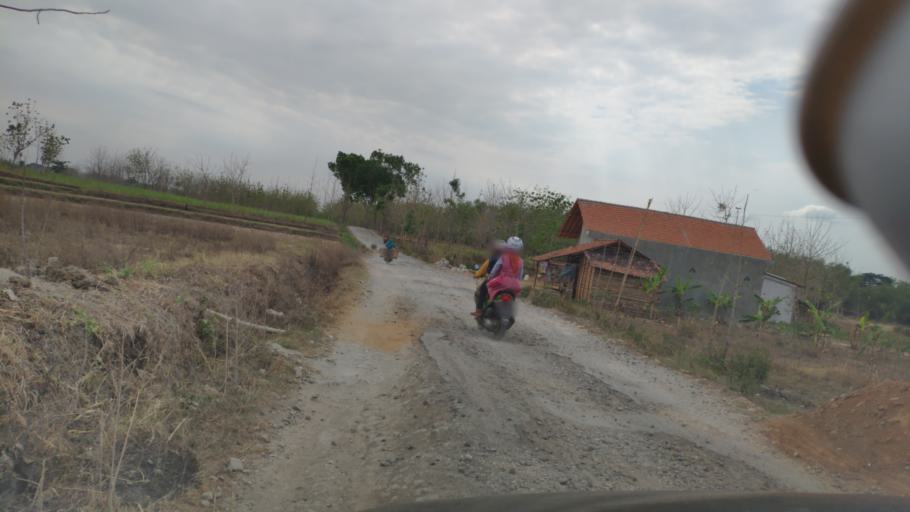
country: ID
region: Central Java
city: Jembangan
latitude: -6.9520
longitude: 111.3842
